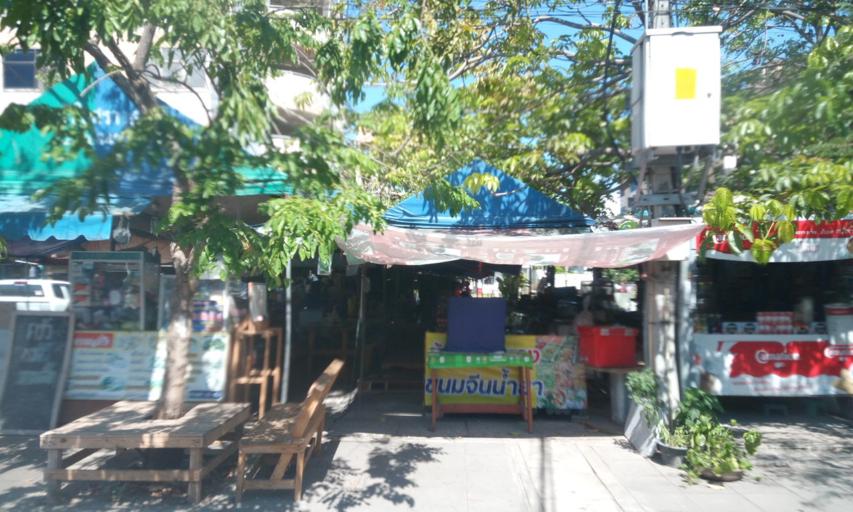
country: TH
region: Samut Prakan
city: Bang Bo District
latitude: 13.5587
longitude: 100.7653
